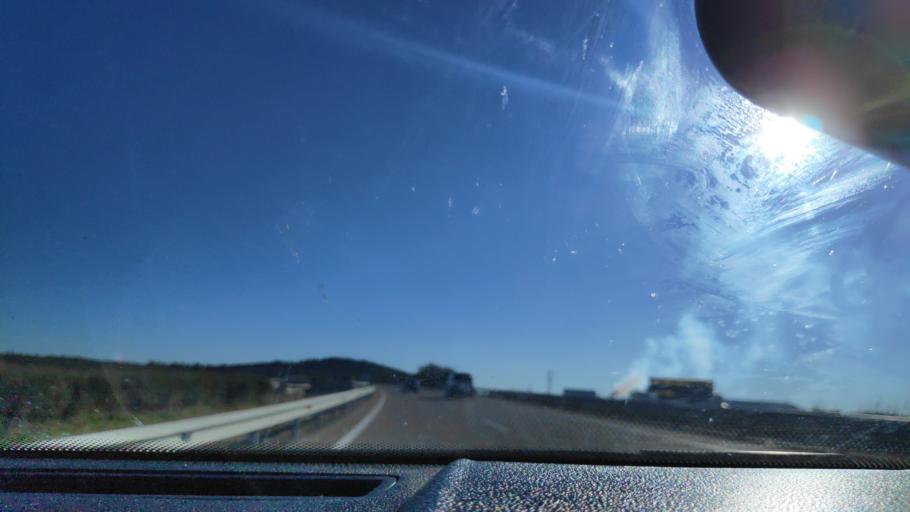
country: ES
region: Extremadura
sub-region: Provincia de Badajoz
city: Los Santos de Maimona
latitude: 38.4731
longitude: -6.3608
